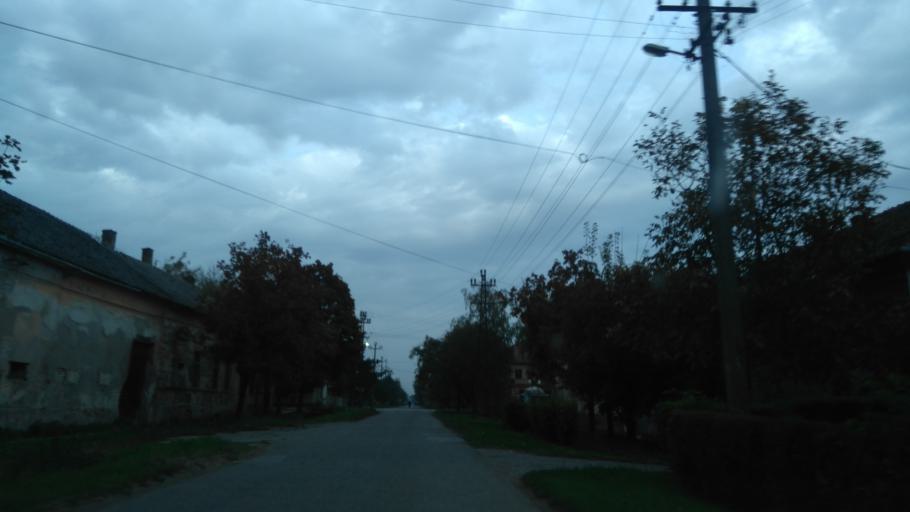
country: RS
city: Mol
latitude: 45.7635
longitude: 20.1363
